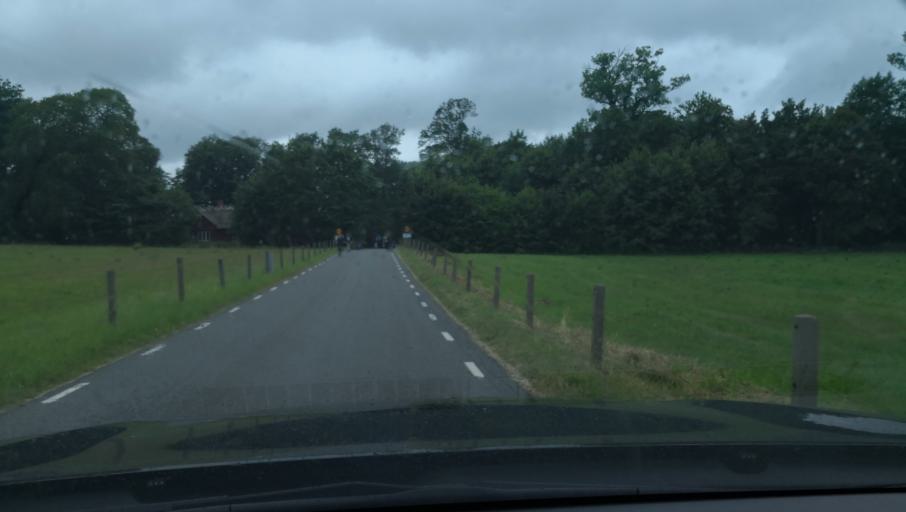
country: SE
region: Skane
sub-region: Simrishamns Kommun
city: Kivik
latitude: 55.6820
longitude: 14.2369
